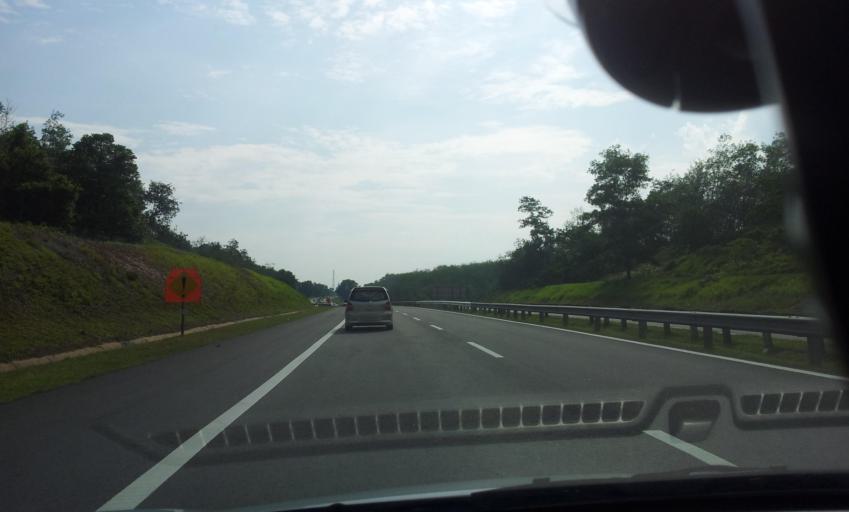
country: MY
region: Pahang
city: Mentekab
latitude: 3.5078
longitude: 102.3597
